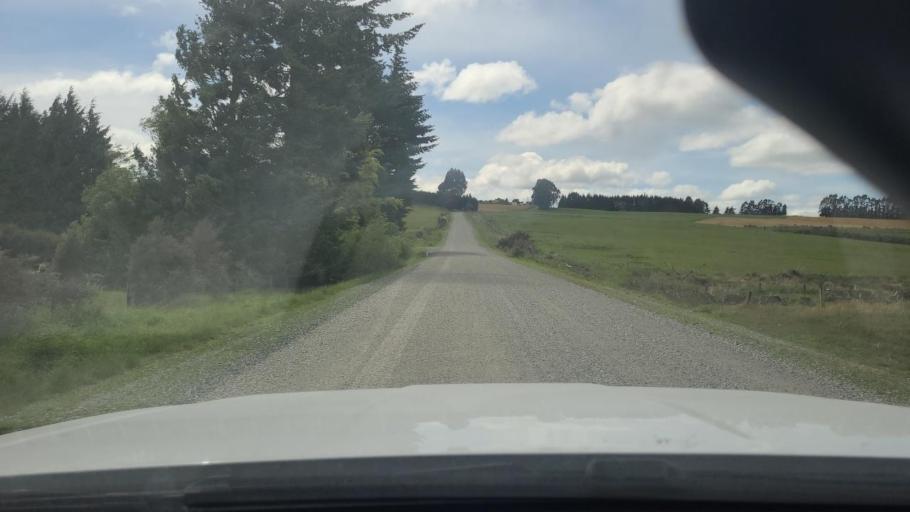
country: NZ
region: Southland
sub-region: Southland District
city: Te Anau
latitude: -45.4804
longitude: 167.9213
